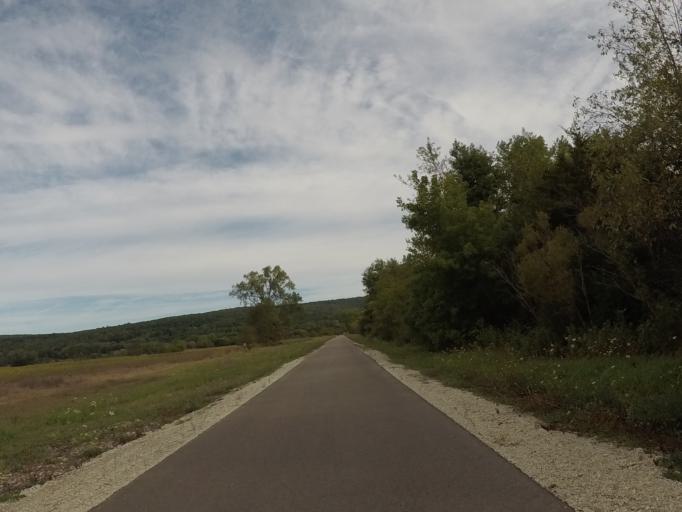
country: US
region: Wisconsin
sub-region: Sauk County
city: Prairie du Sac
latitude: 43.3719
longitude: -89.7356
